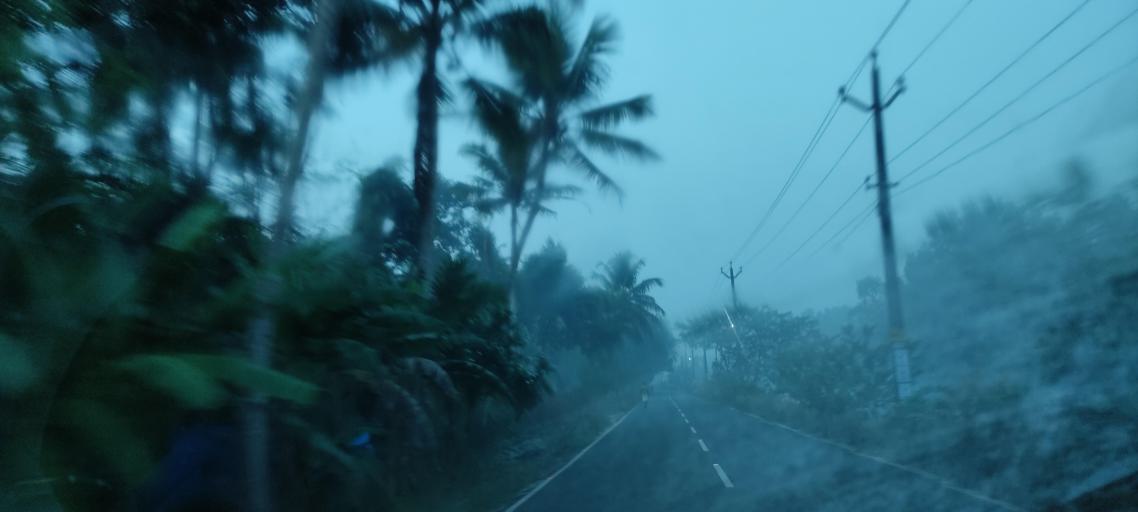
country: IN
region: Kerala
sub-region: Alappuzha
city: Alleppey
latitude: 9.5881
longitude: 76.3328
